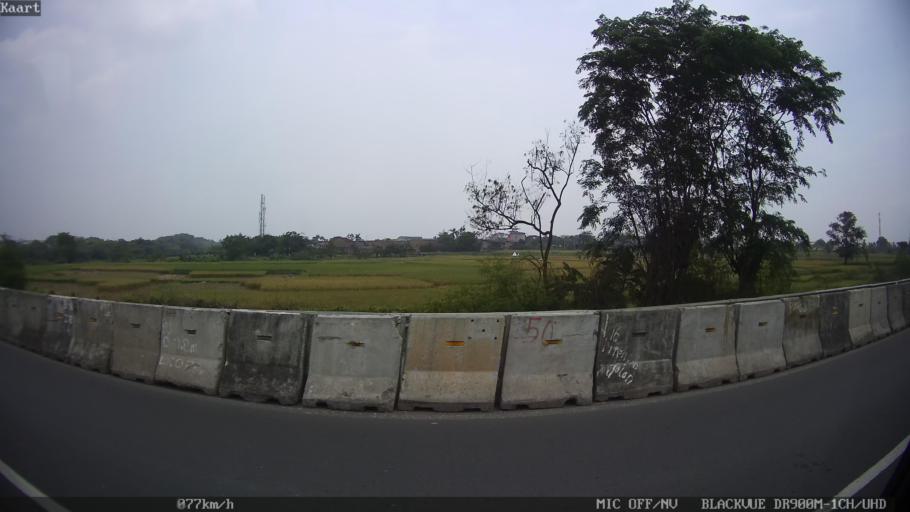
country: ID
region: West Java
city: Kresek
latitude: -6.1537
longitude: 106.3207
